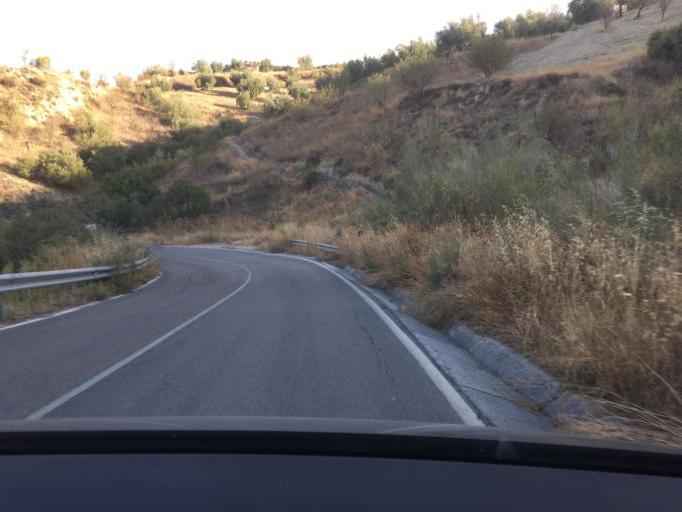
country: ES
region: Andalusia
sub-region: Provincia de Granada
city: Quentar
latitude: 37.1953
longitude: -3.4711
